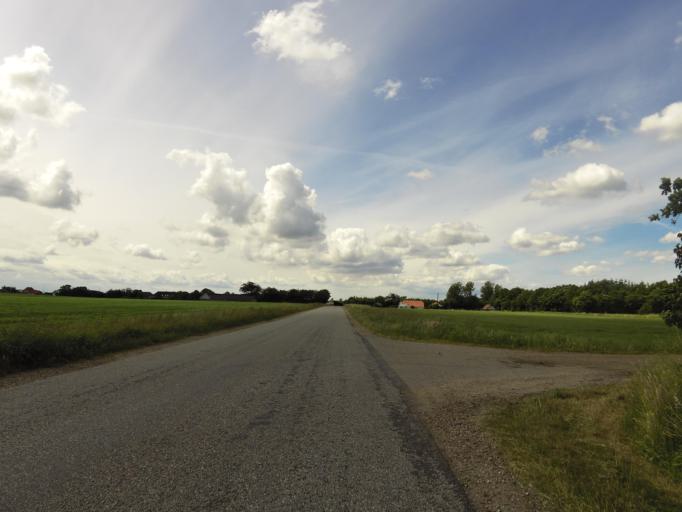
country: DK
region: South Denmark
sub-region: Esbjerg Kommune
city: Ribe
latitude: 55.2602
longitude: 8.8287
